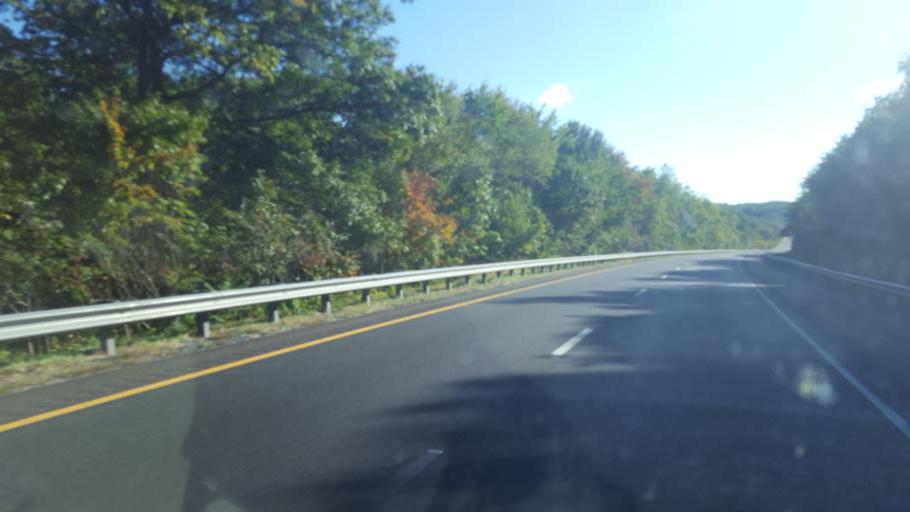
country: US
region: Maryland
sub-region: Washington County
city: Wilson-Conococheague
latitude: 39.6270
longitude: -77.9834
